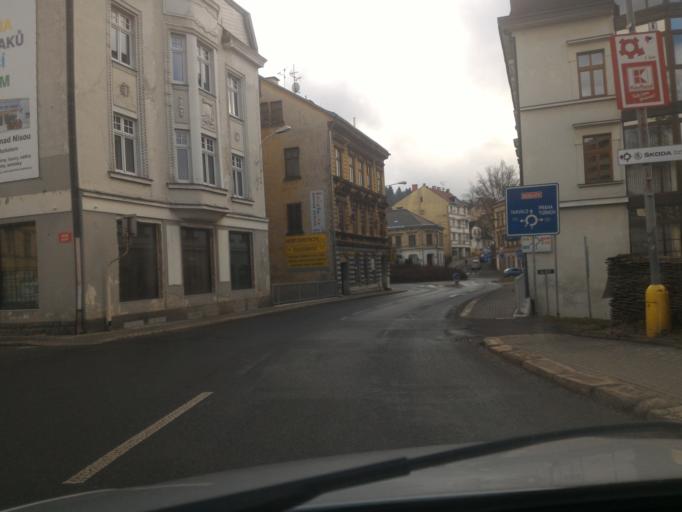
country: CZ
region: Liberecky
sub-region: Okres Jablonec nad Nisou
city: Jablonec nad Nisou
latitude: 50.7220
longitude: 15.1683
